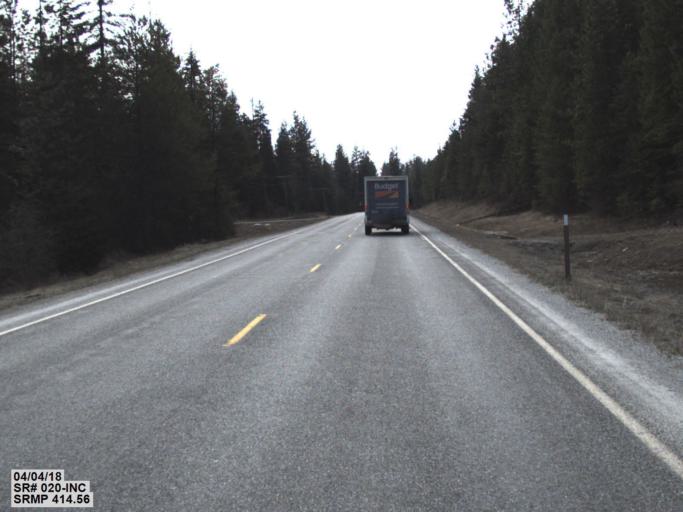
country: US
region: Washington
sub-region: Pend Oreille County
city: Newport
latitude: 48.4007
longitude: -117.3139
